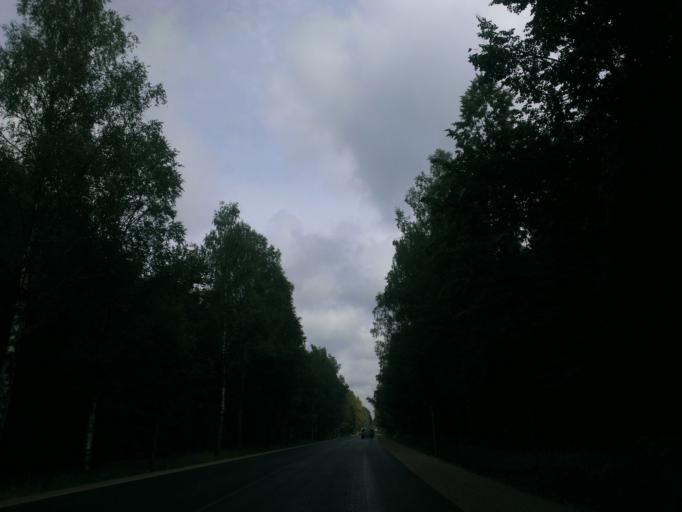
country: LV
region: Amatas Novads
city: Drabesi
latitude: 57.2138
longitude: 25.1811
